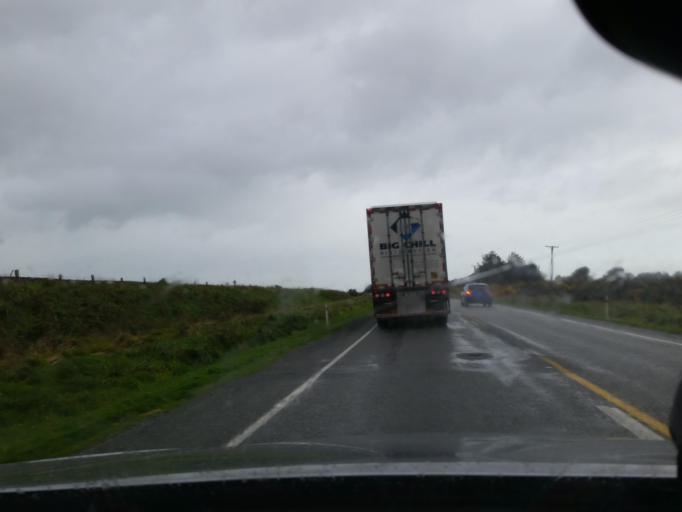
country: NZ
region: Southland
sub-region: Invercargill City
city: Invercargill
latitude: -46.4688
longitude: 168.3808
